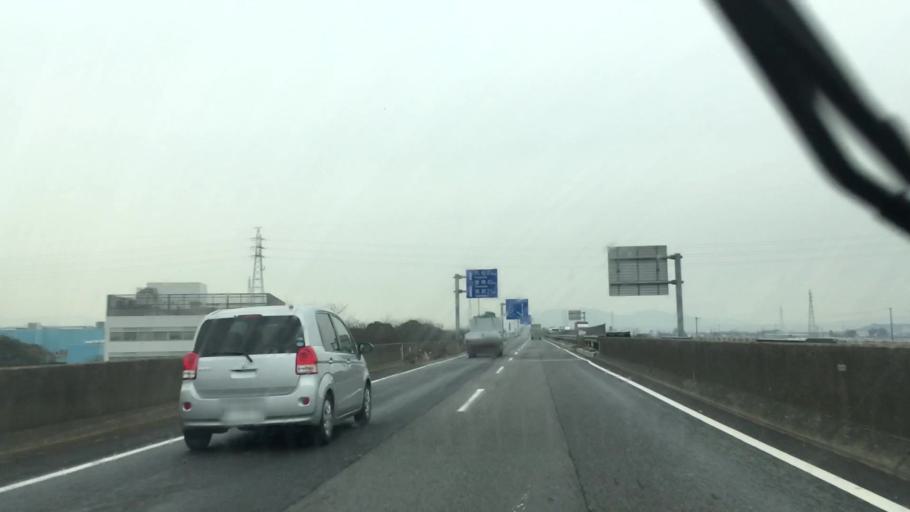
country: JP
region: Aichi
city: Nishio
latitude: 34.9048
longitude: 137.0651
